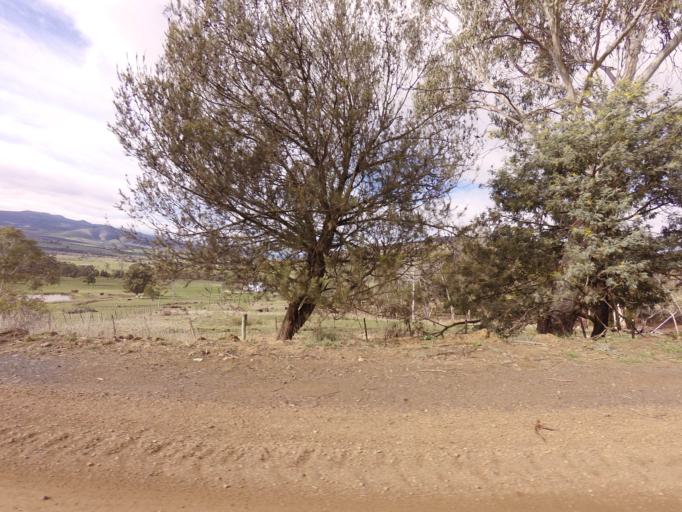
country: AU
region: Tasmania
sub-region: Derwent Valley
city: New Norfolk
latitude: -42.7220
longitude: 146.8732
